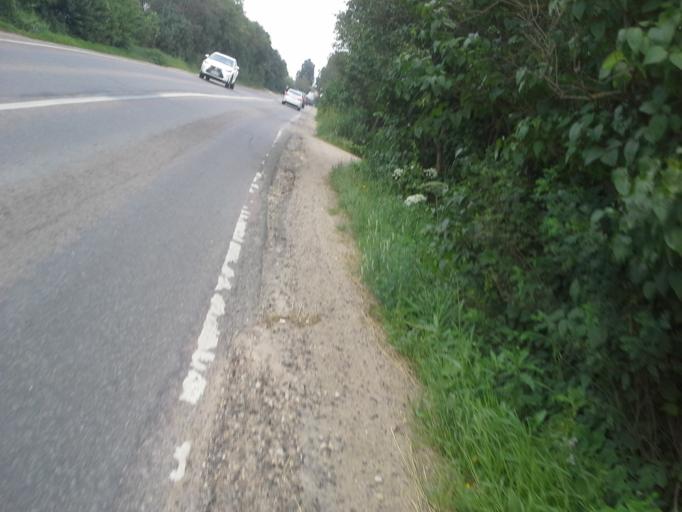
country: RU
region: Moskovskaya
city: Istra
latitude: 55.9299
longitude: 36.9084
